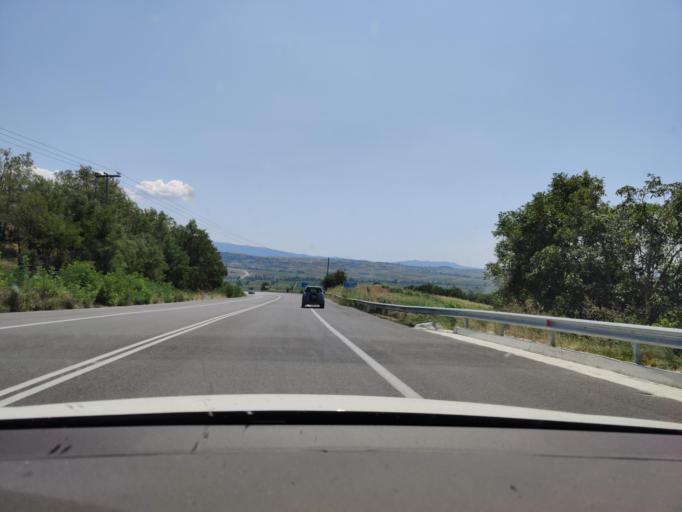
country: GR
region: Central Macedonia
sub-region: Nomos Serron
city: Draviskos
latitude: 40.9798
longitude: 23.8629
